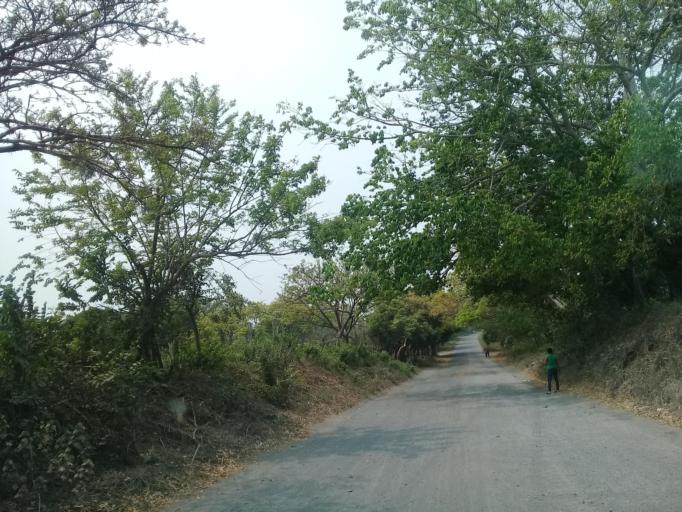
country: MX
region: Veracruz
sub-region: Medellin
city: La Laguna y Monte del Castillo
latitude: 18.9461
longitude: -96.1263
